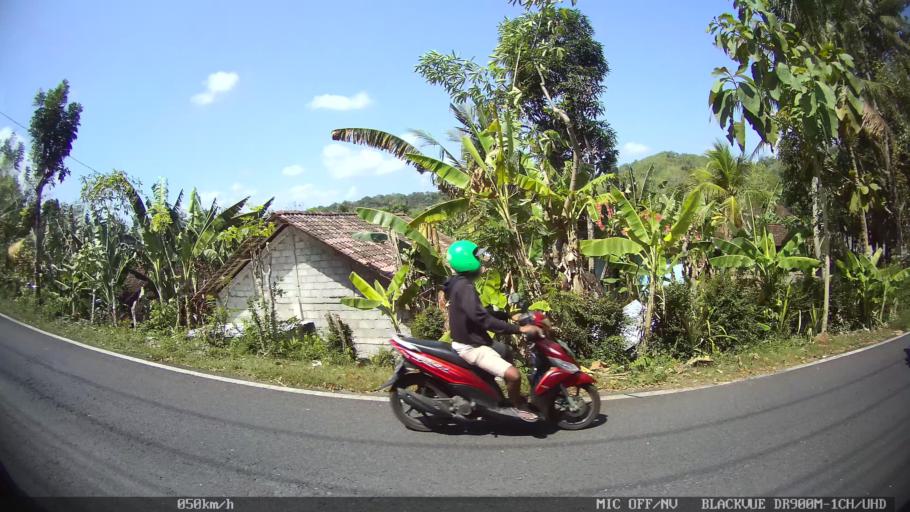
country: ID
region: Daerah Istimewa Yogyakarta
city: Pundong
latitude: -7.9586
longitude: 110.3744
